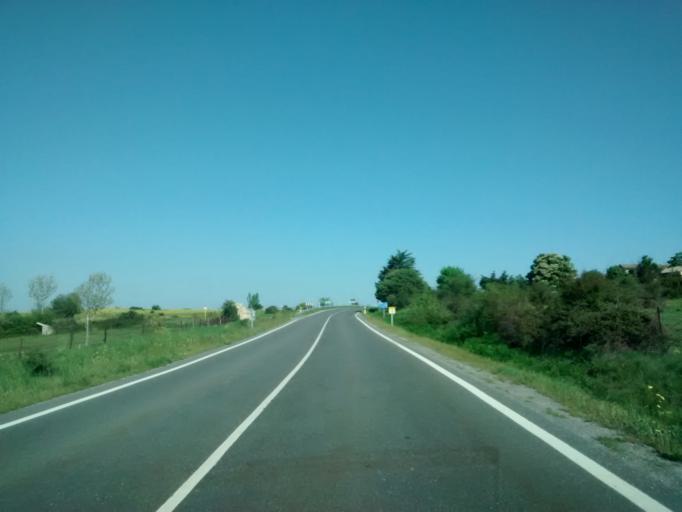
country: ES
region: Castille and Leon
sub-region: Provincia de Segovia
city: San Ildefonso
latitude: 40.9216
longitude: -4.0239
